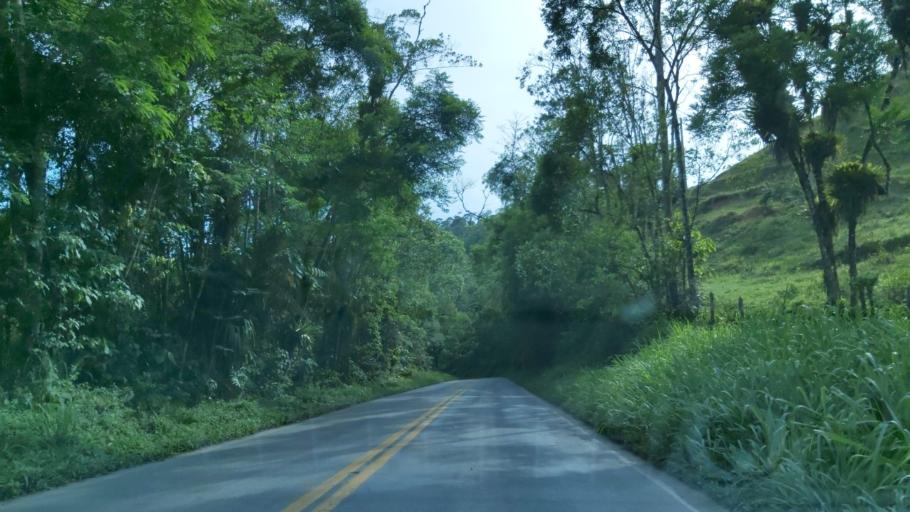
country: BR
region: Sao Paulo
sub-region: Miracatu
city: Miracatu
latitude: -24.0568
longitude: -47.5861
